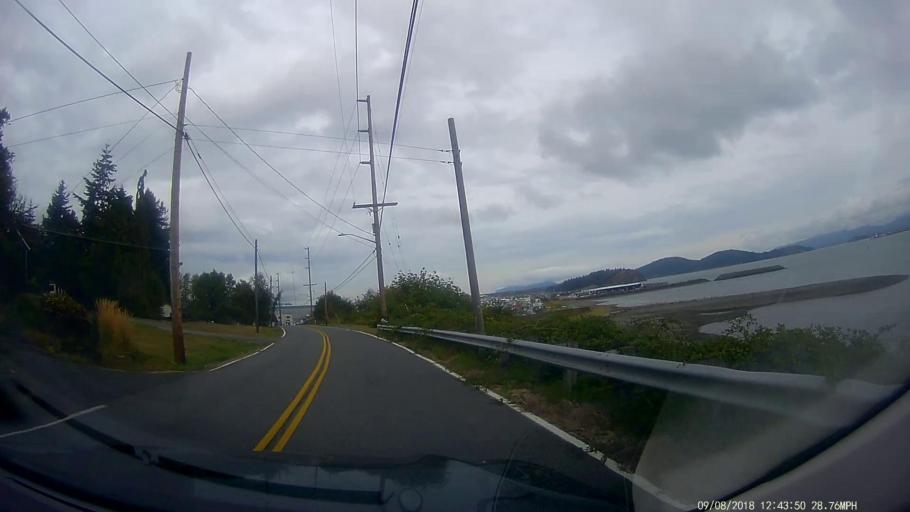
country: US
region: Washington
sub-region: Skagit County
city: Anacortes
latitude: 48.4924
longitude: -122.6006
